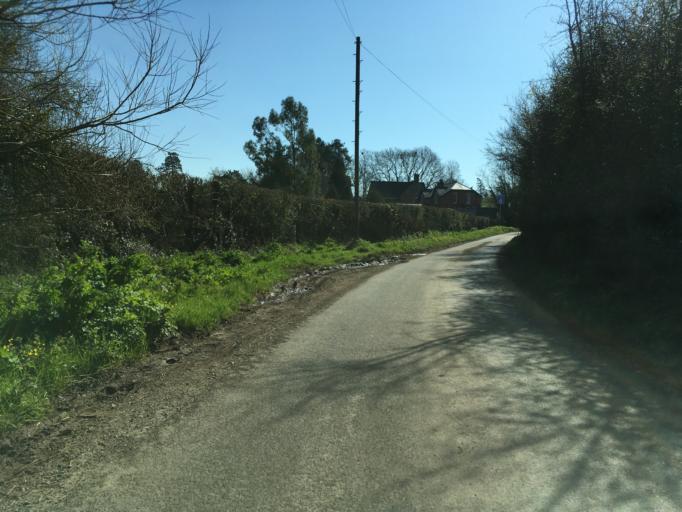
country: GB
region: England
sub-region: Gloucestershire
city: Berkeley
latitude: 51.6855
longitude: -2.4665
